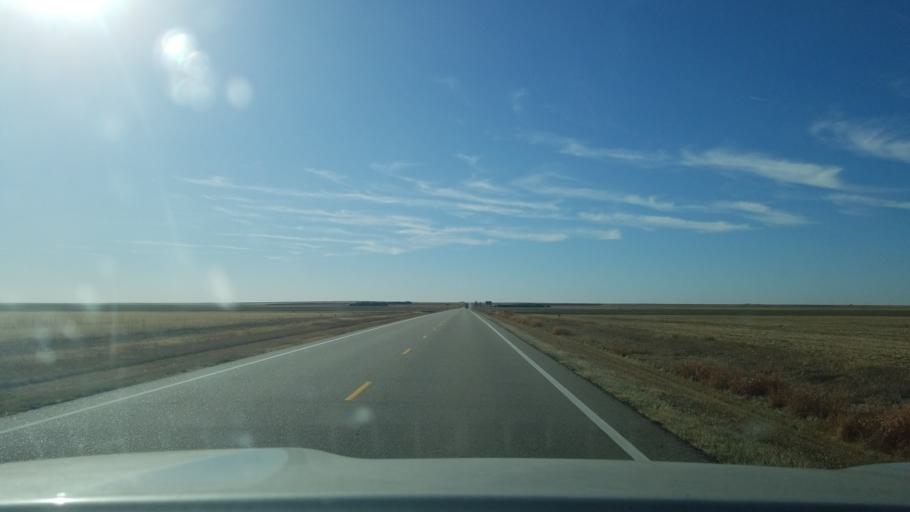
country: US
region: Kansas
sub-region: Ness County
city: Ness City
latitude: 38.3808
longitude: -99.8983
